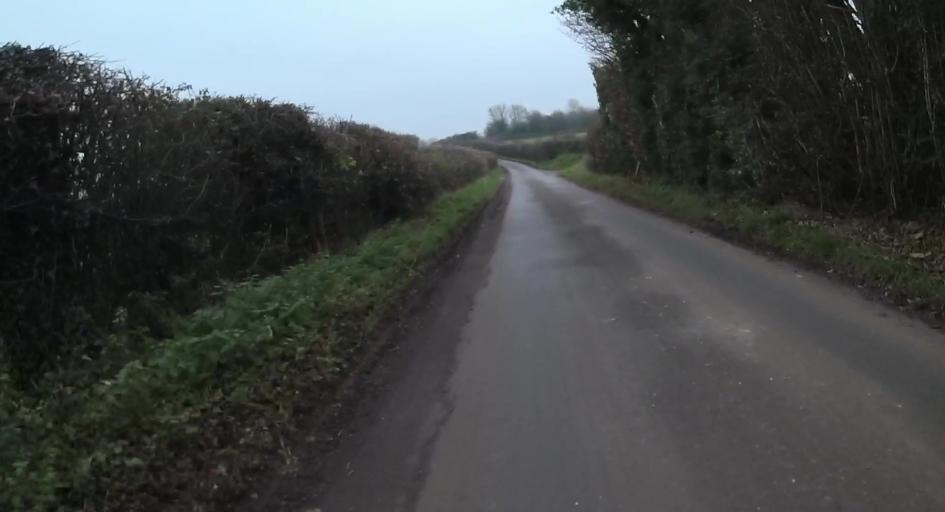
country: GB
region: England
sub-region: Hampshire
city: Kings Worthy
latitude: 51.1149
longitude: -1.2114
